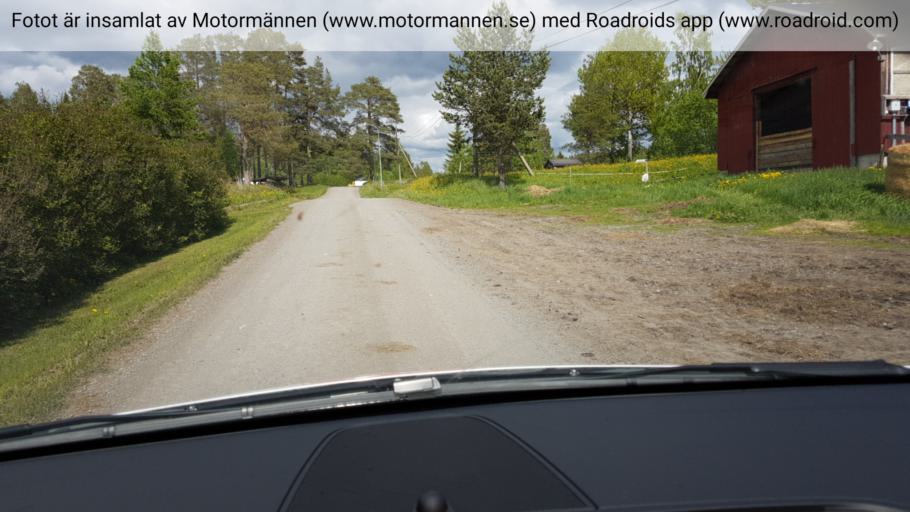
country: SE
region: Jaemtland
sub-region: OEstersunds Kommun
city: Brunflo
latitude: 62.9758
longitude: 14.6841
